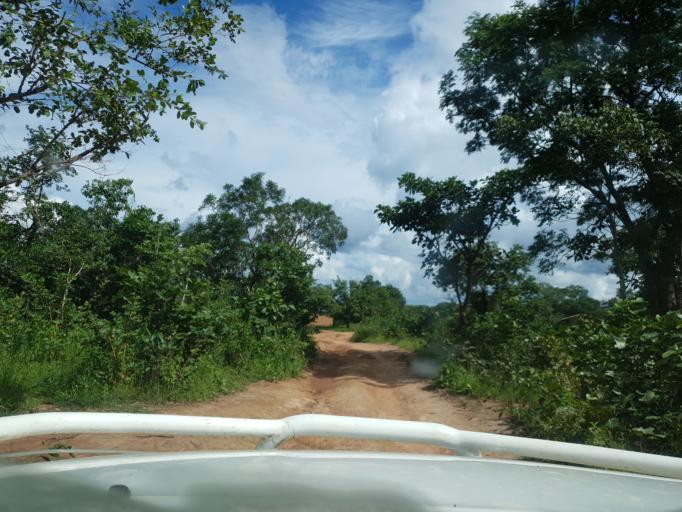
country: CI
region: Savanes
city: Tengrela
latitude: 10.4587
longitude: -6.7956
